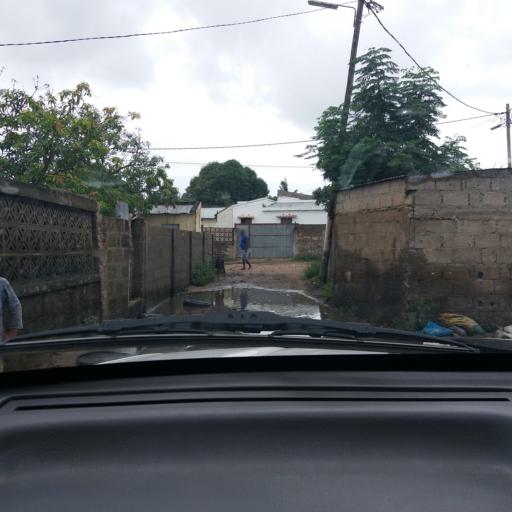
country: MZ
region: Maputo City
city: Maputo
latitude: -25.9043
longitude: 32.5943
